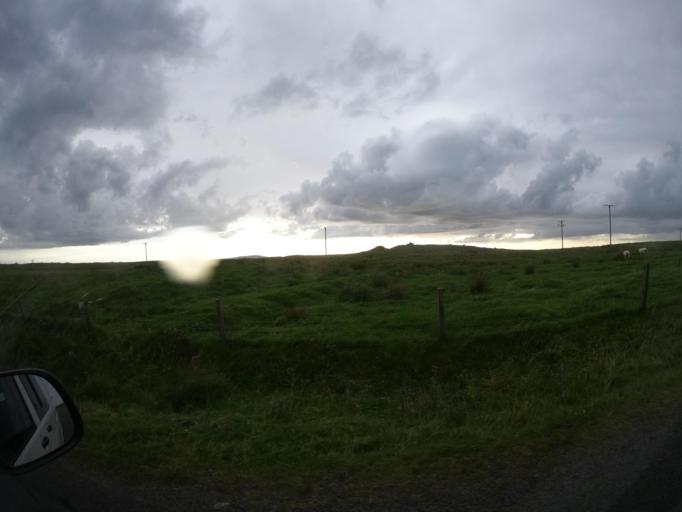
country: GB
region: Scotland
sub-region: Eilean Siar
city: Barra
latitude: 56.5090
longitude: -6.8108
